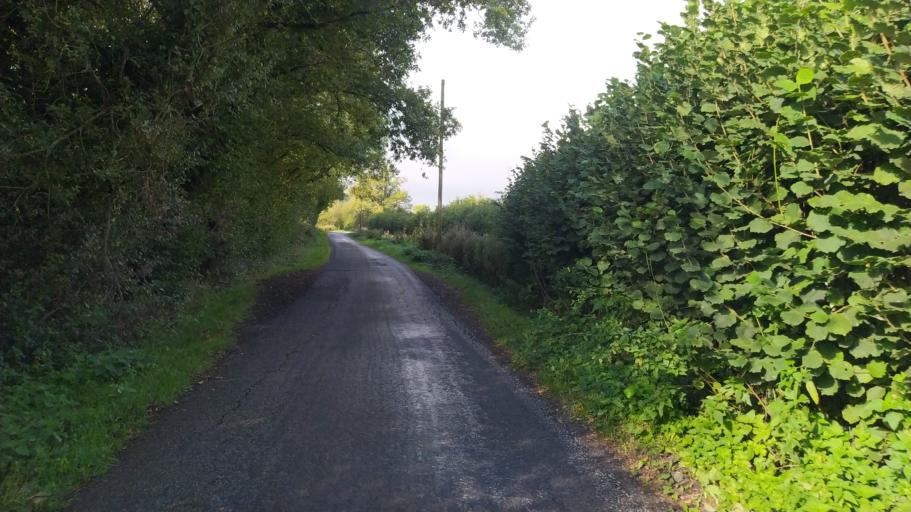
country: GB
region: England
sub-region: Wiltshire
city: Hindon
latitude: 51.0388
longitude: -2.1437
